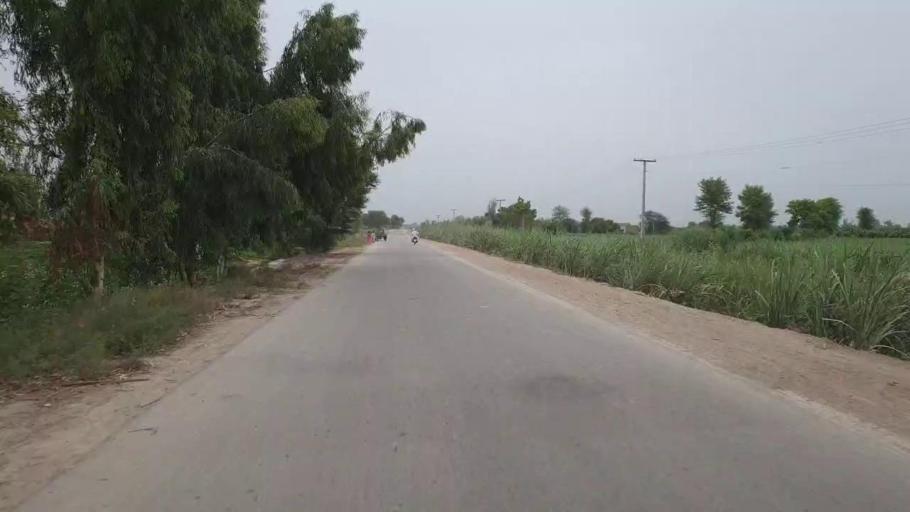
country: PK
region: Sindh
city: Bandhi
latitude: 26.5529
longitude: 68.2116
